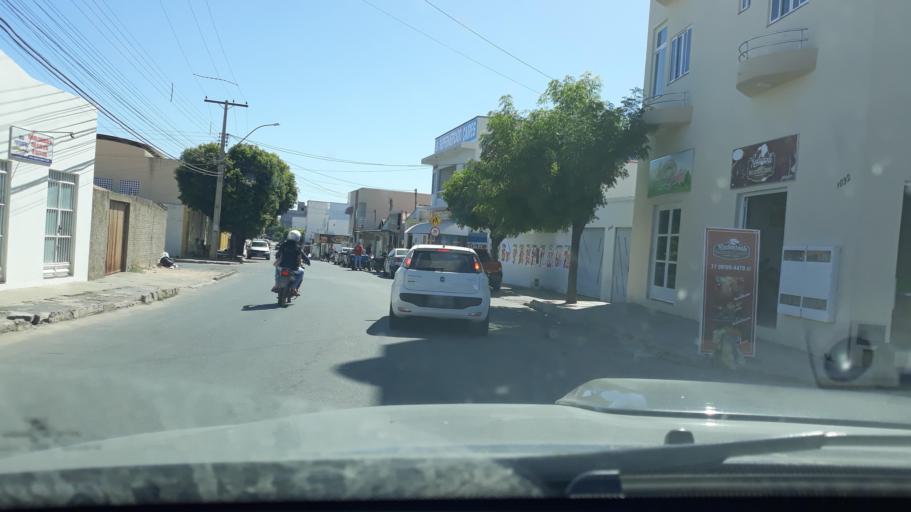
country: BR
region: Bahia
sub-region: Guanambi
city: Guanambi
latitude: -14.2236
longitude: -42.7904
